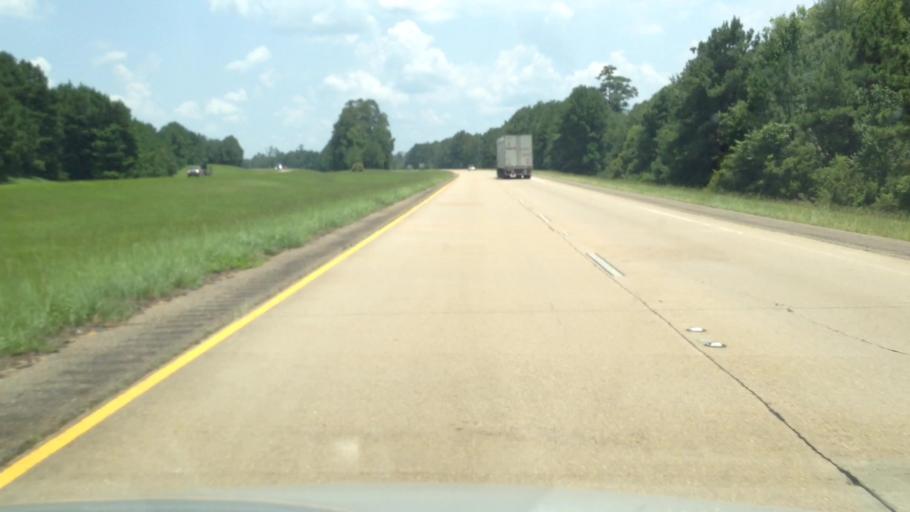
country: US
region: Louisiana
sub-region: Rapides Parish
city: Lecompte
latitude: 31.0392
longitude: -92.4155
